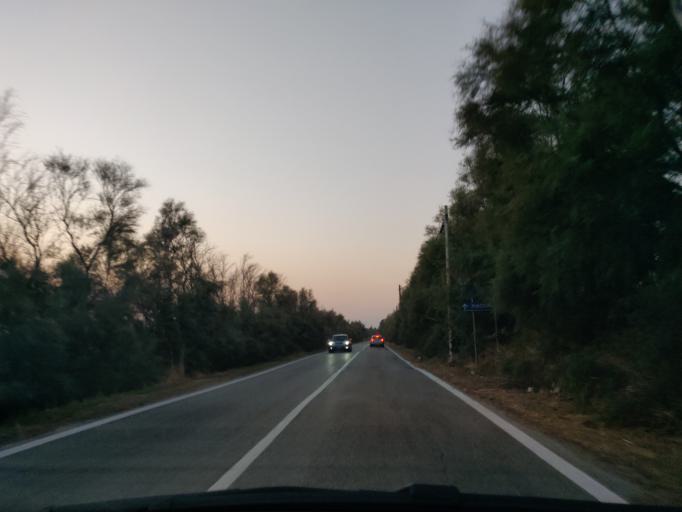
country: IT
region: Latium
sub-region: Citta metropolitana di Roma Capitale
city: Npp 23 (Parco Leonardo)
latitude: 41.8218
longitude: 12.2931
